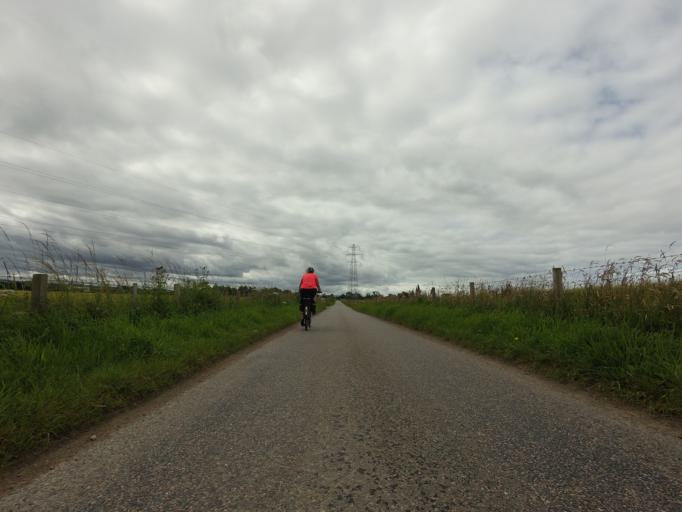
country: GB
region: Scotland
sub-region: Moray
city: Forres
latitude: 57.6196
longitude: -3.6147
